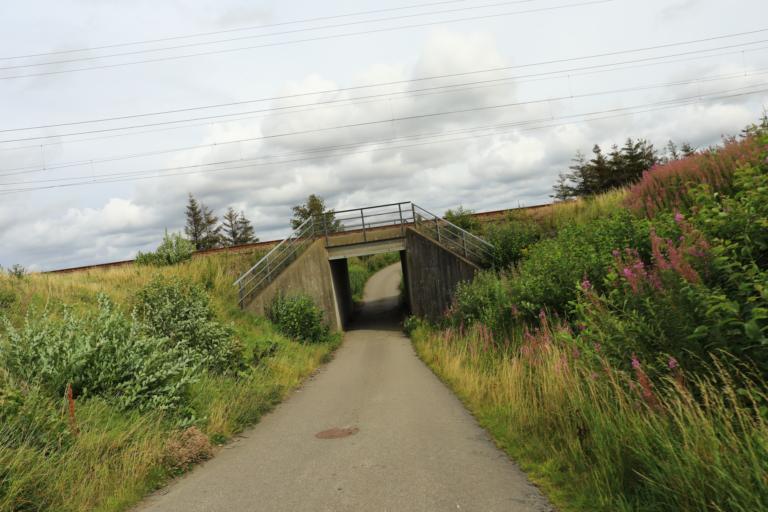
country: SE
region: Halland
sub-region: Varbergs Kommun
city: Varberg
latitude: 57.1438
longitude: 12.2559
